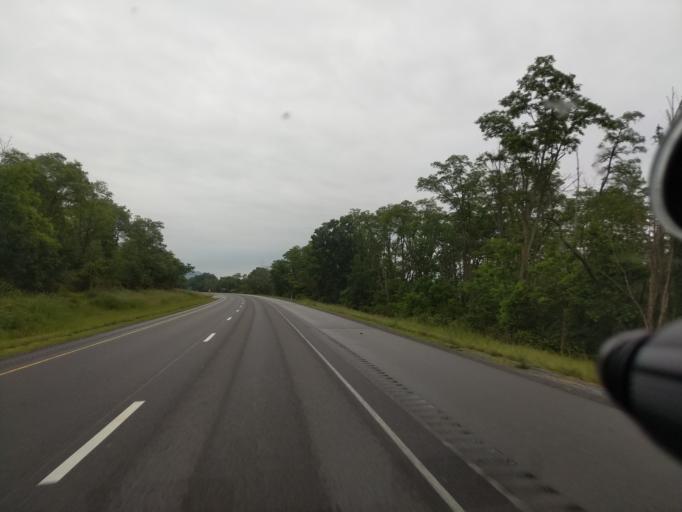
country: US
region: Pennsylvania
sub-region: Clinton County
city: Castanea
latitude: 41.0638
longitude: -77.4265
